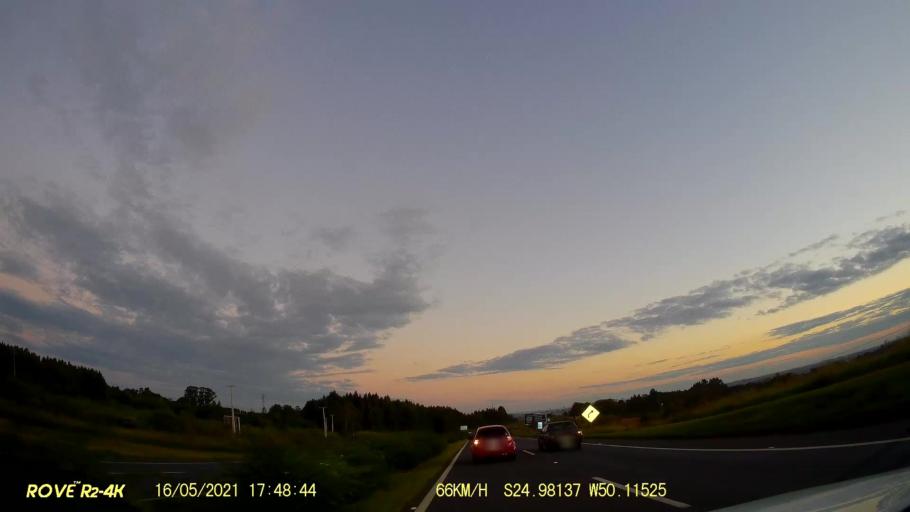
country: BR
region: Parana
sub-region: Carambei
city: Carambei
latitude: -24.9809
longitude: -50.1165
